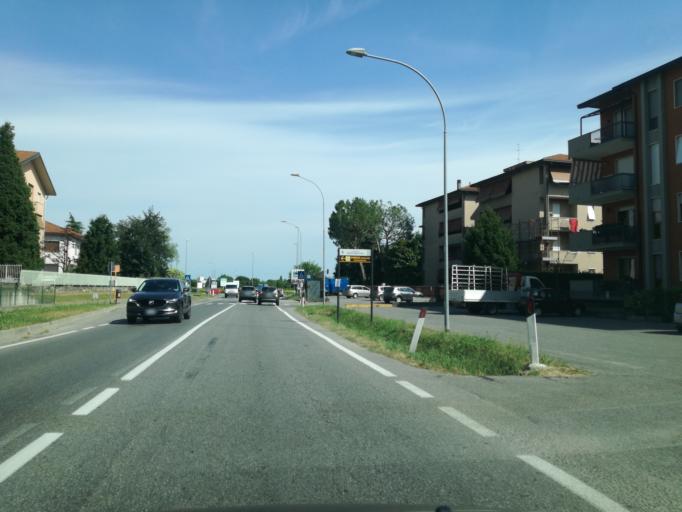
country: IT
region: Lombardy
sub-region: Provincia di Monza e Brianza
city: Bernareggio
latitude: 45.6453
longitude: 9.4020
